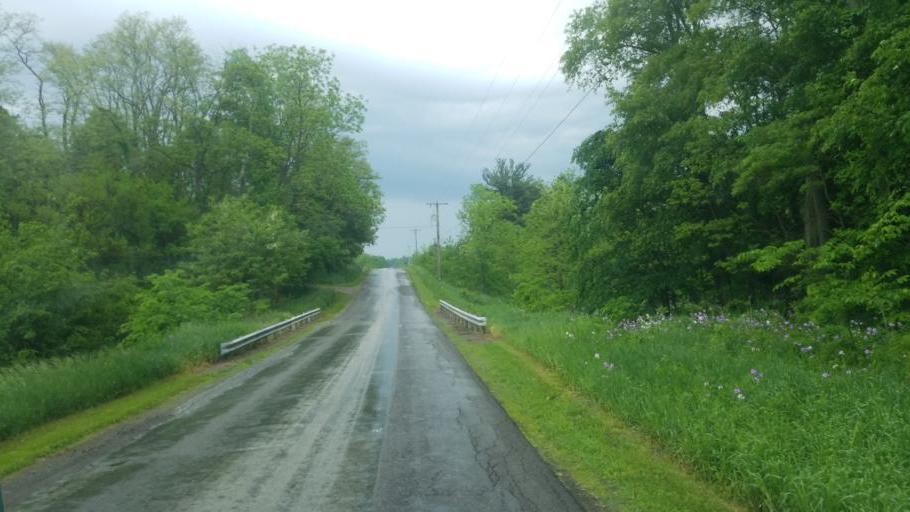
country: US
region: Ohio
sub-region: Wayne County
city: Dalton
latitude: 40.7728
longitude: -81.7069
